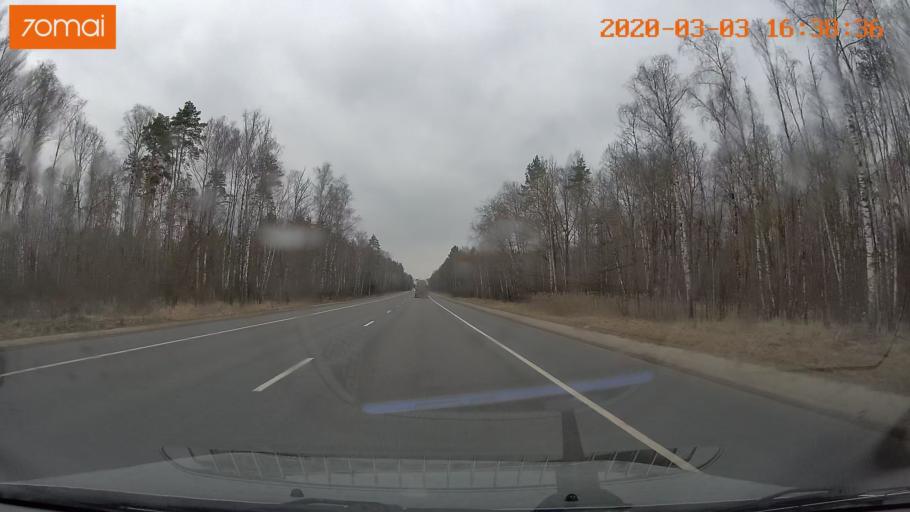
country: RU
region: Moskovskaya
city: Lopatinskiy
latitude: 55.3869
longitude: 38.7644
